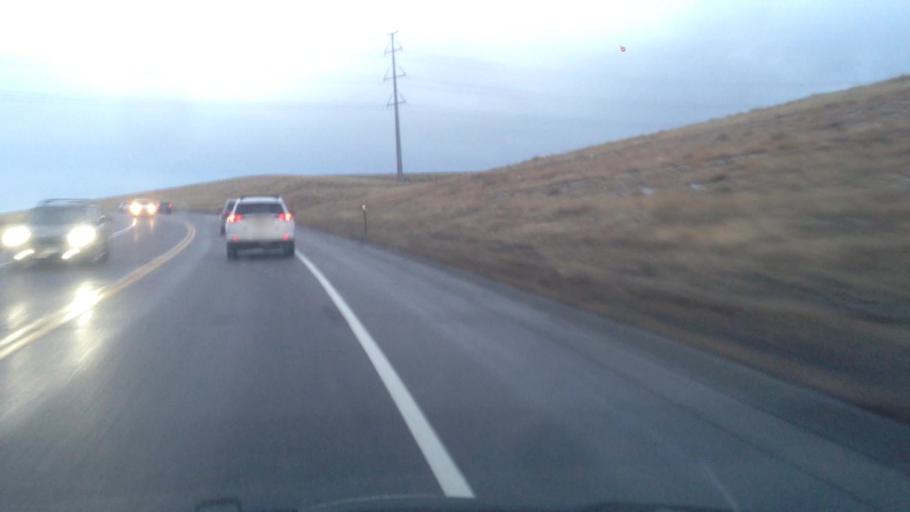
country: US
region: Colorado
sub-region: Douglas County
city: Meridian
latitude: 39.5199
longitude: -104.8496
